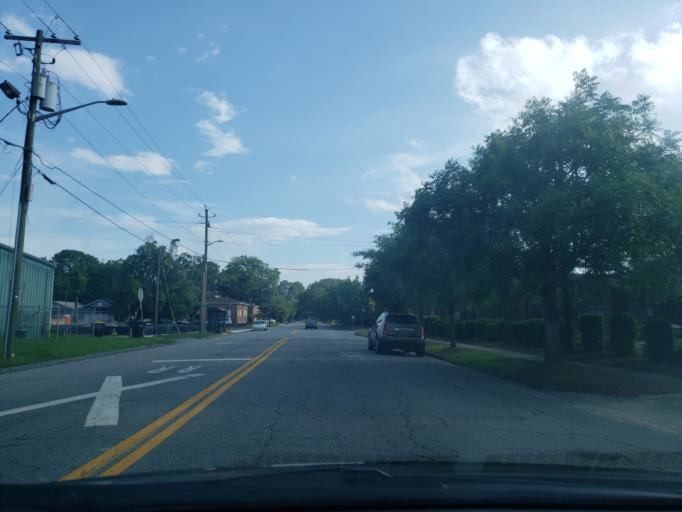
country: US
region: Georgia
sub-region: Chatham County
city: Savannah
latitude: 32.0506
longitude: -81.1049
